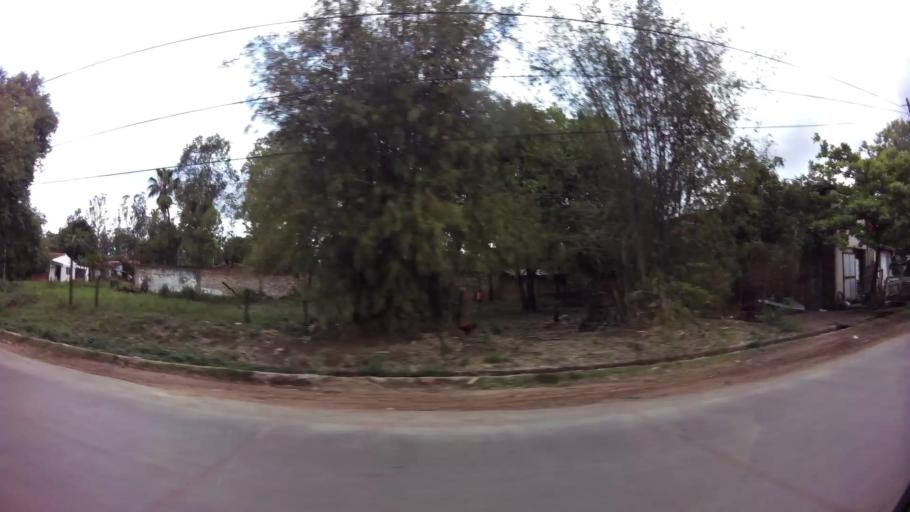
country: PY
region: Central
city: Fernando de la Mora
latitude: -25.2865
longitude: -57.5167
